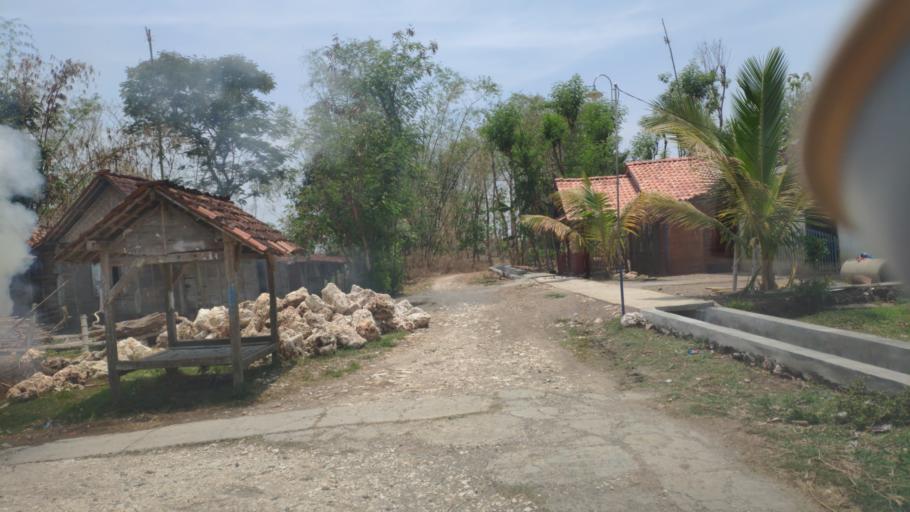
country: ID
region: Central Java
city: Kendayakan
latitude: -7.0594
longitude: 111.3048
